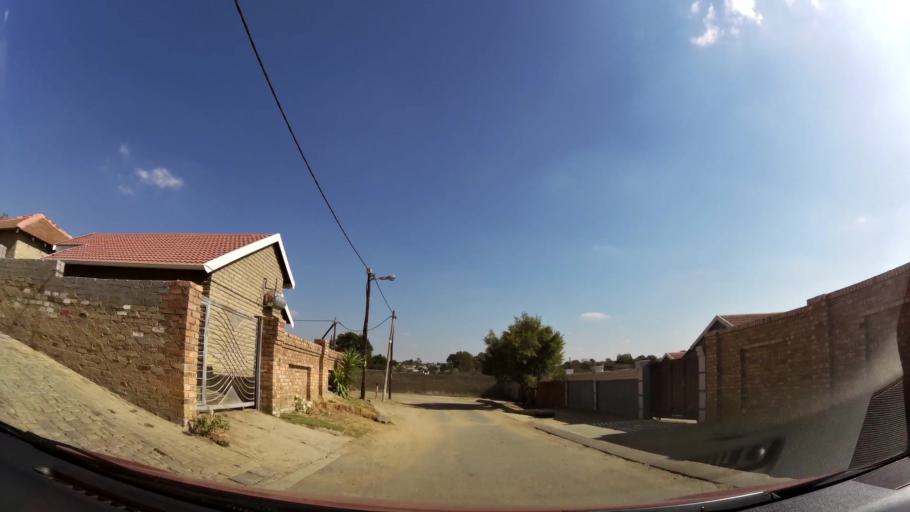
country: ZA
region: Gauteng
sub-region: West Rand District Municipality
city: Muldersdriseloop
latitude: -26.0147
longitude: 27.9342
